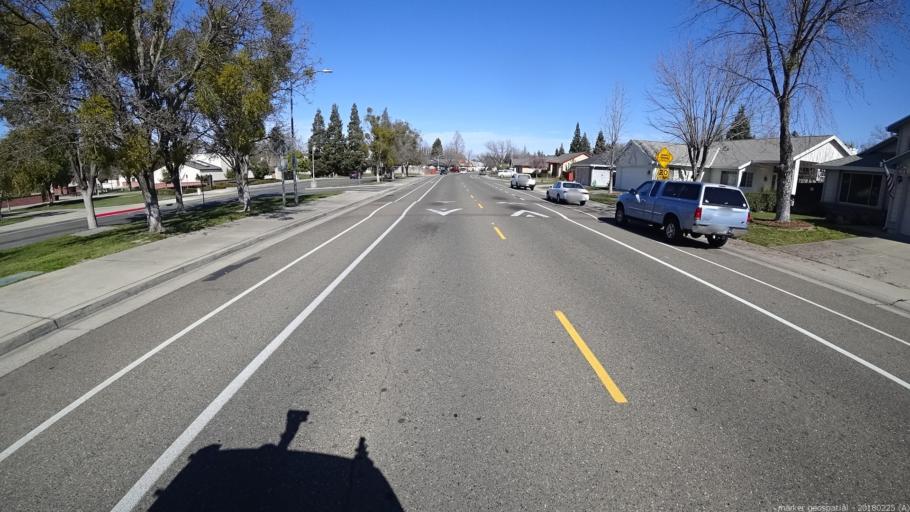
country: US
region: California
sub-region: Sacramento County
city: Antelope
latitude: 38.7184
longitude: -121.3397
